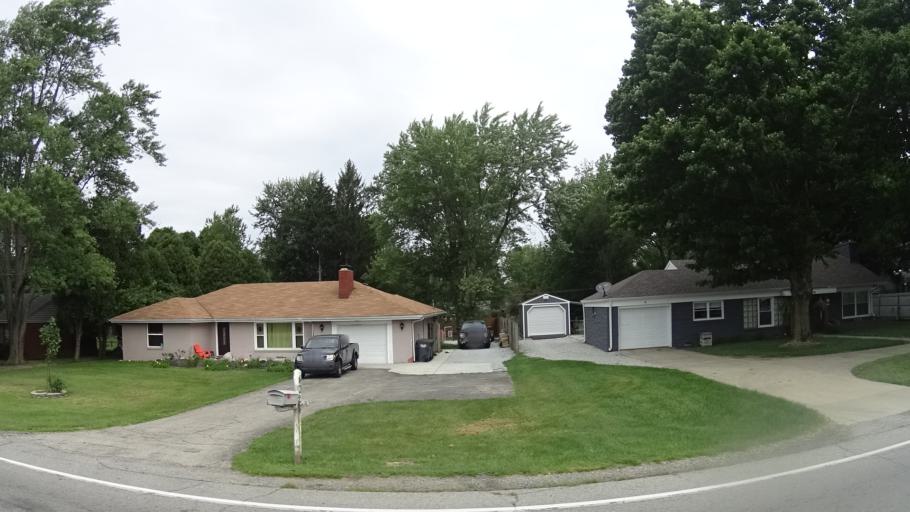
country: US
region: Indiana
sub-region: Madison County
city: Edgewood
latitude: 40.1016
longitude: -85.7419
